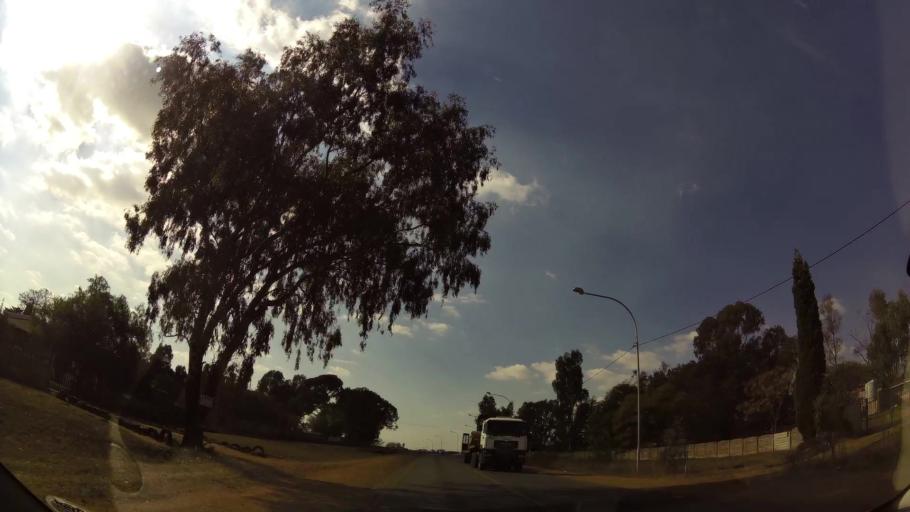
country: ZA
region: Gauteng
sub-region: Ekurhuleni Metropolitan Municipality
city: Benoni
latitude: -26.1024
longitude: 28.3469
